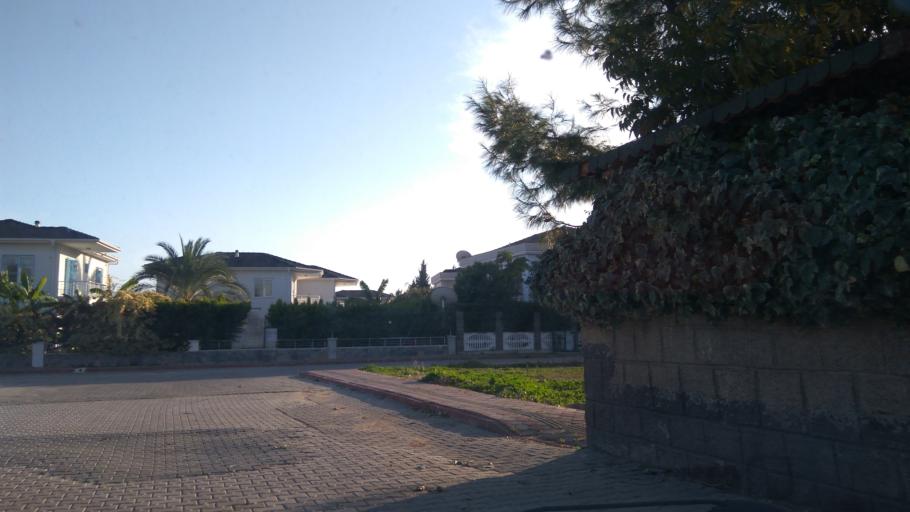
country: TR
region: Antalya
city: Kemer
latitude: 36.5659
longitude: 30.5600
